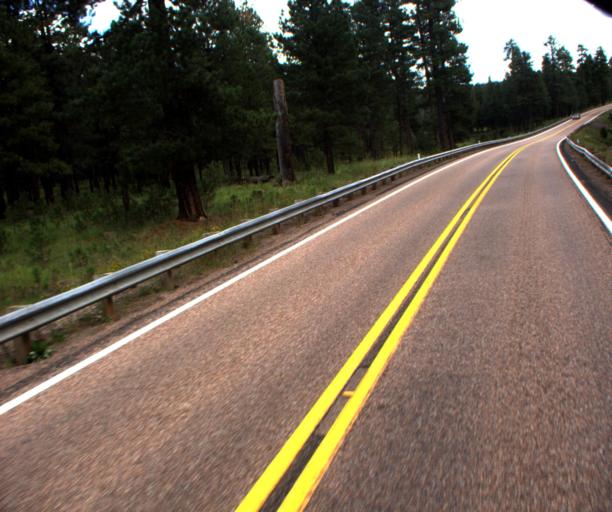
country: US
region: Arizona
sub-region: Navajo County
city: Pinetop-Lakeside
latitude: 34.0369
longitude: -109.6662
